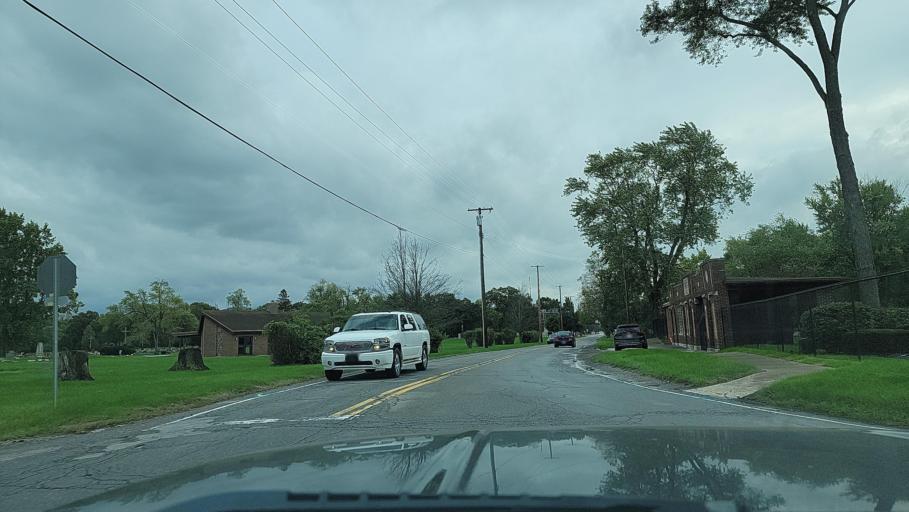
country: US
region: Indiana
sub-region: Porter County
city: Portage
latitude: 41.5750
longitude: -87.2025
